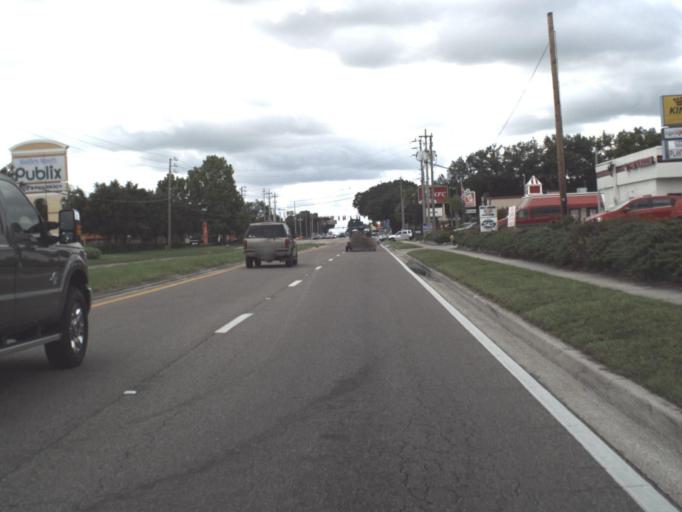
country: US
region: Florida
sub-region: Hillsborough County
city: Plant City
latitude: 27.9918
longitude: -82.1217
